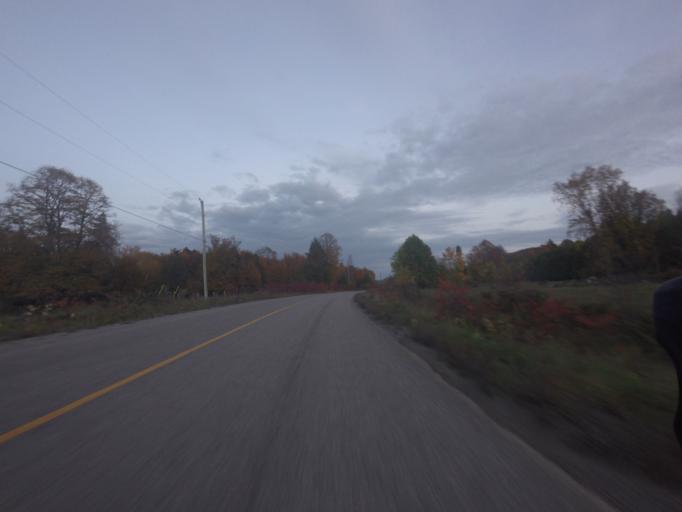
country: CA
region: Ontario
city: Renfrew
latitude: 45.3488
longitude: -76.9424
